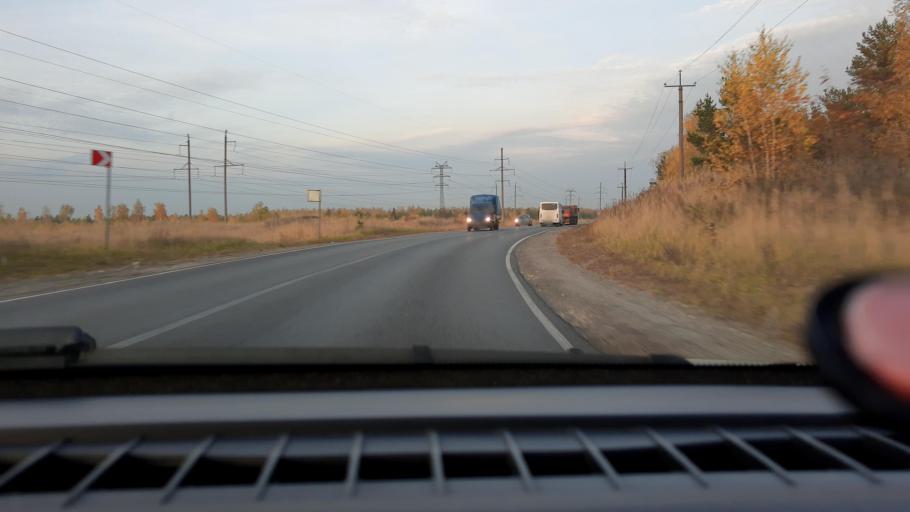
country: RU
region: Nizjnij Novgorod
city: Babino
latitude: 56.3265
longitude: 43.5592
